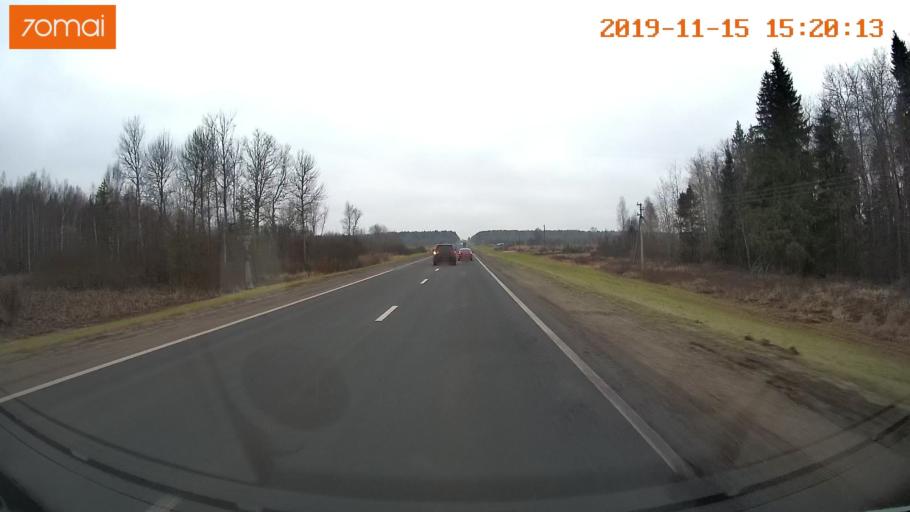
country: RU
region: Jaroslavl
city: Danilov
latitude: 58.2260
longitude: 40.1653
